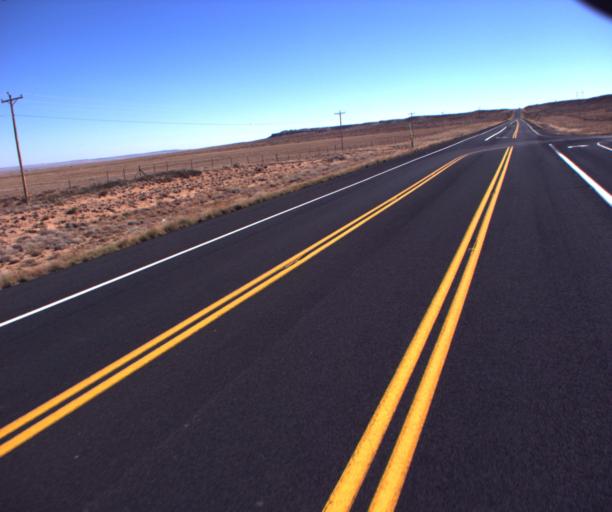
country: US
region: Arizona
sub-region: Coconino County
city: Tuba City
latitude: 35.9982
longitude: -111.0312
